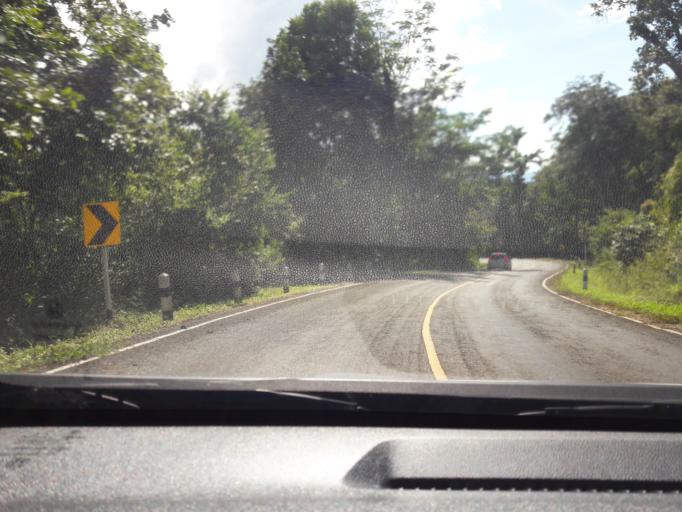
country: TH
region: Mae Hong Son
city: Sop Pong
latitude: 19.5738
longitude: 98.2034
